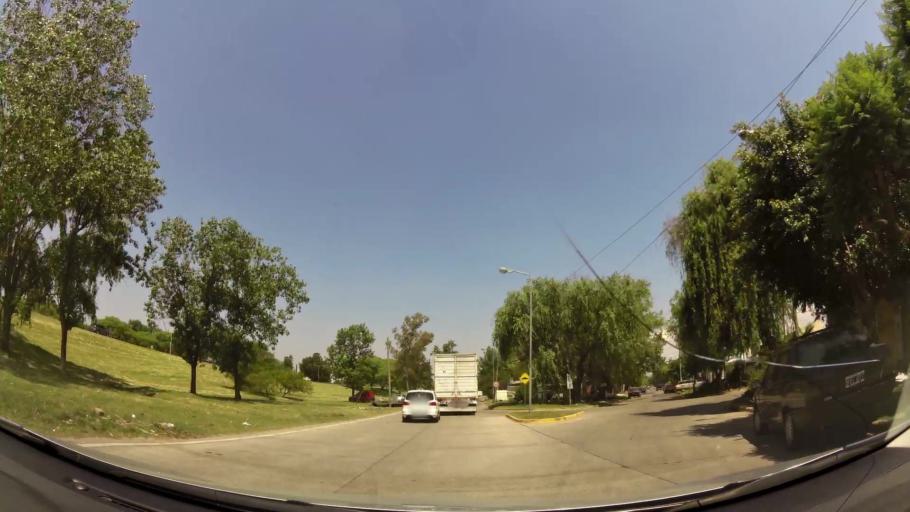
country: AR
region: Buenos Aires
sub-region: Partido de Tigre
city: Tigre
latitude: -34.4421
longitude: -58.5825
